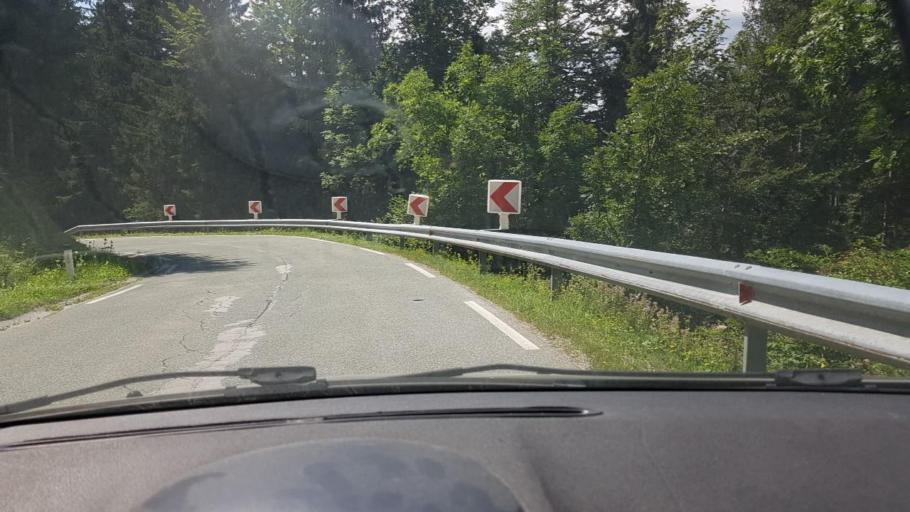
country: SI
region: Jezersko
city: Zgornje Jezersko
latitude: 46.4099
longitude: 14.5282
